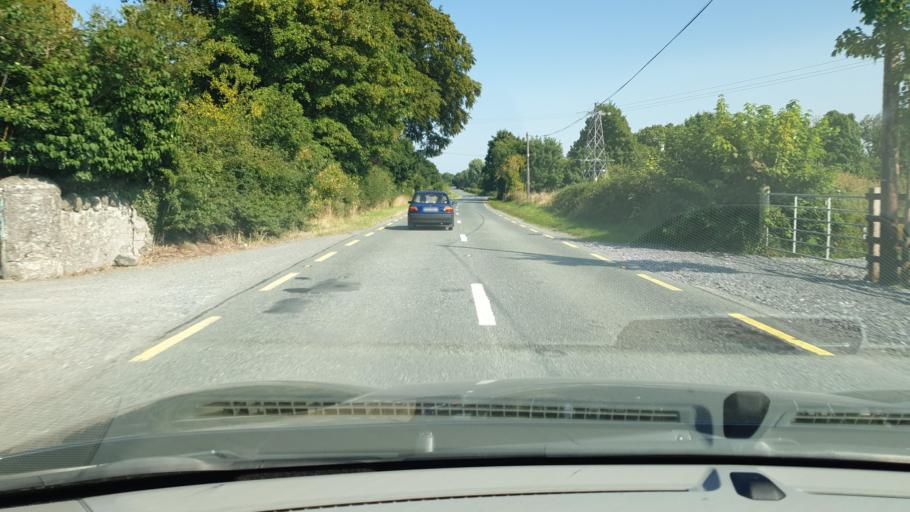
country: IE
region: Leinster
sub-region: An Mhi
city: Trim
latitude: 53.6316
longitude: -6.7989
